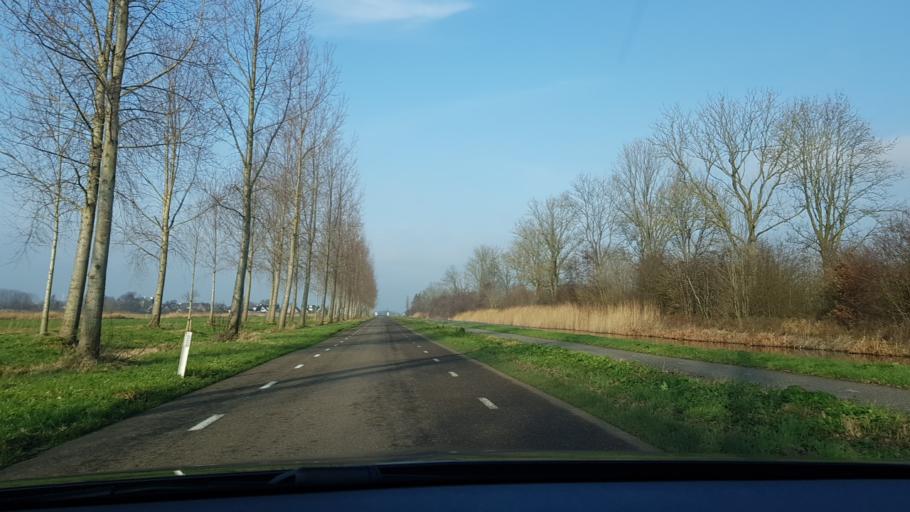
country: NL
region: Utrecht
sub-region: Gemeente De Ronde Venen
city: Mijdrecht
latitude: 52.1906
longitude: 4.9183
